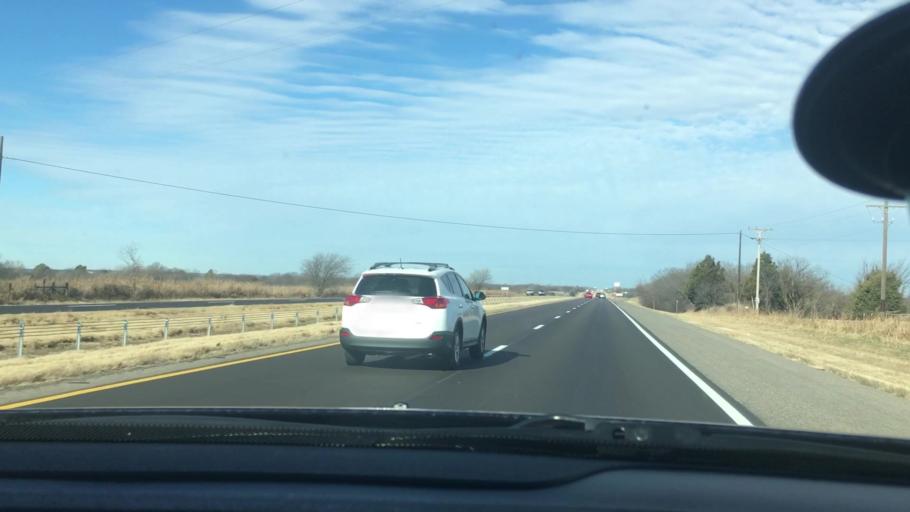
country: US
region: Oklahoma
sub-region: Cleveland County
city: Noble
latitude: 35.0956
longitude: -97.4233
